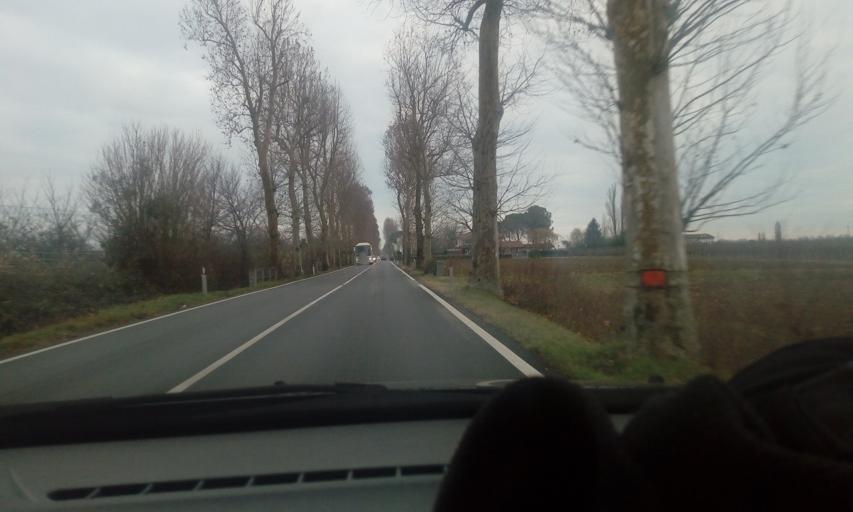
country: IT
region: Friuli Venezia Giulia
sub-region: Provincia di Udine
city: Terzo d'Aquileia
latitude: 45.7915
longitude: 13.3558
